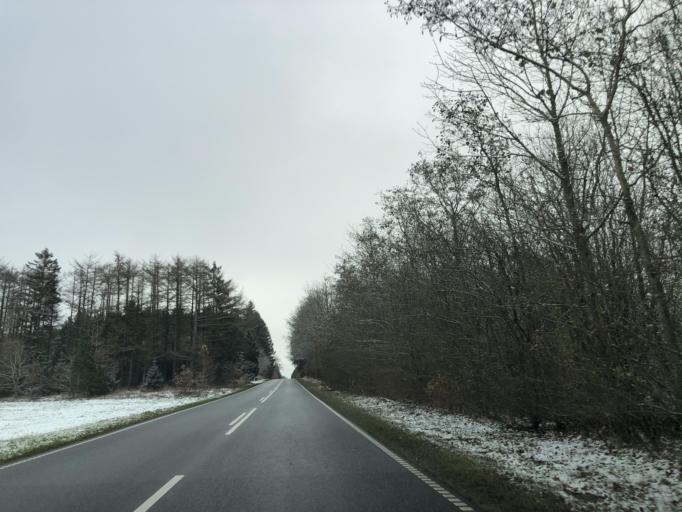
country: DK
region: Central Jutland
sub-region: Ikast-Brande Kommune
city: Brande
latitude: 55.9866
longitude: 9.2401
